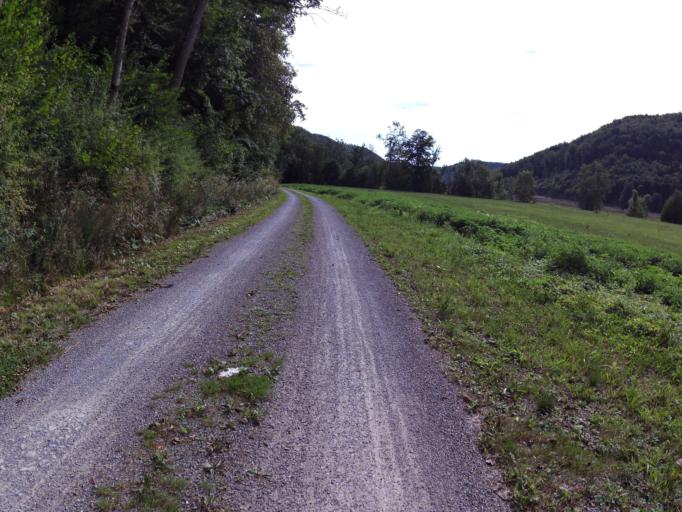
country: DE
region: Baden-Wuerttemberg
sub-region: Freiburg Region
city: Sulz am Neckar
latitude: 48.3487
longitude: 8.5935
